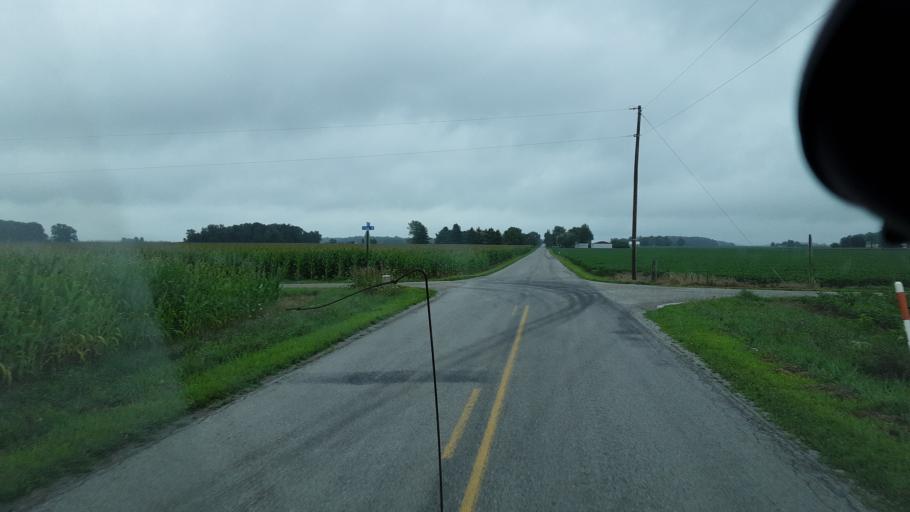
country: US
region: Indiana
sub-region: Wells County
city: Ossian
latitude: 40.9033
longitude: -85.1096
